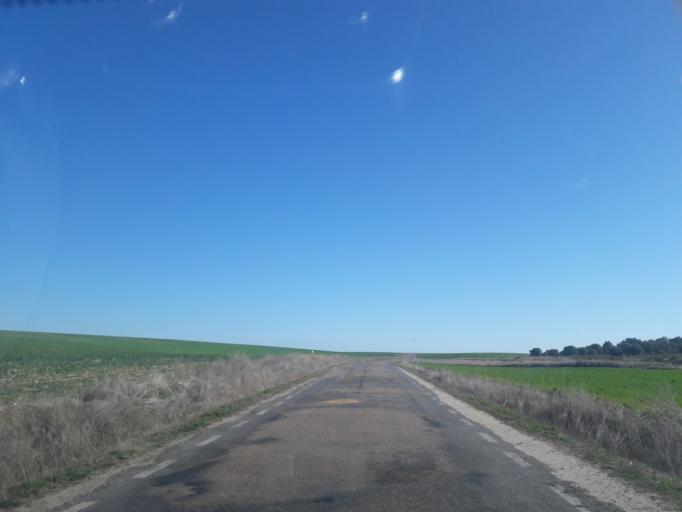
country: ES
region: Castille and Leon
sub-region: Provincia de Salamanca
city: Tordillos
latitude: 40.8643
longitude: -5.3378
